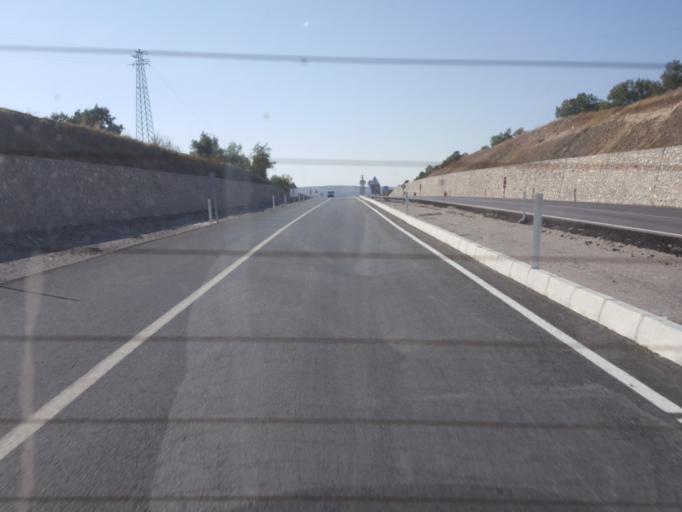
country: TR
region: Corum
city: Seydim
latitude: 40.5856
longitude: 34.7512
